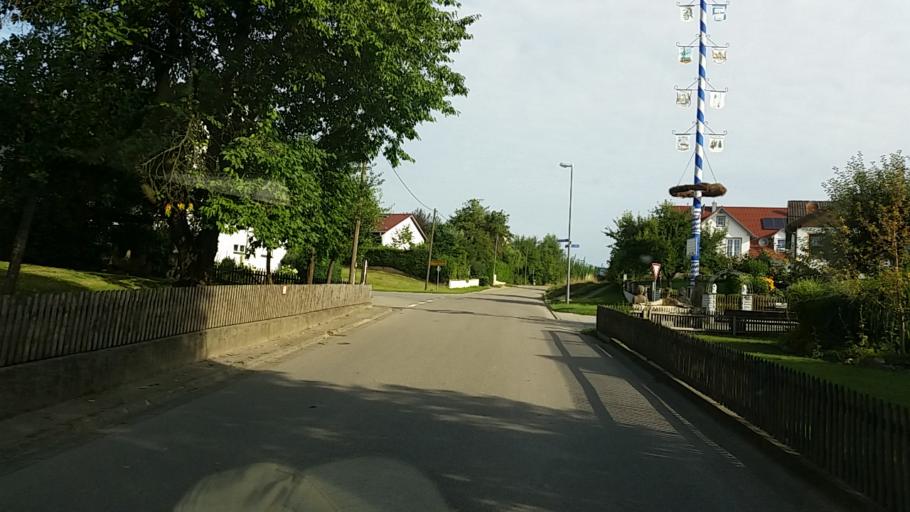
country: DE
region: Bavaria
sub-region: Upper Bavaria
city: Schweitenkirchen
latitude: 48.5052
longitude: 11.6529
